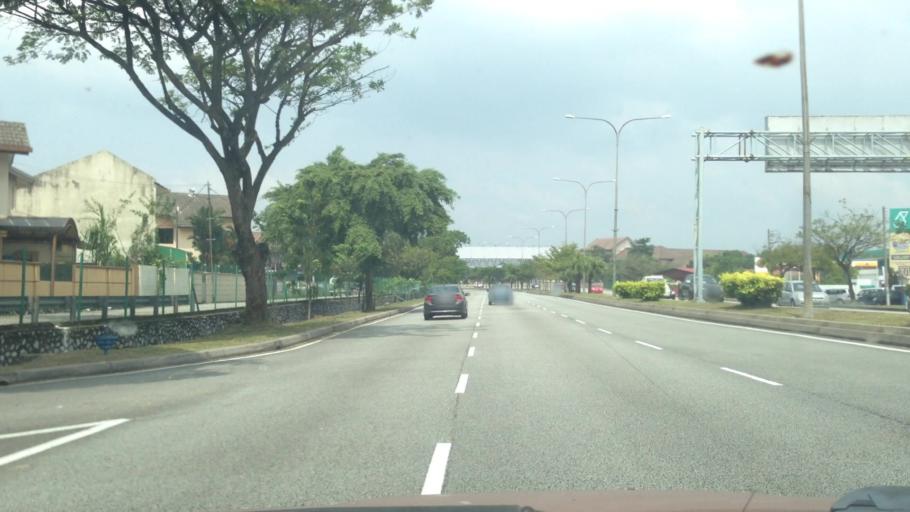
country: MY
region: Selangor
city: Subang Jaya
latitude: 3.0572
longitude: 101.5781
